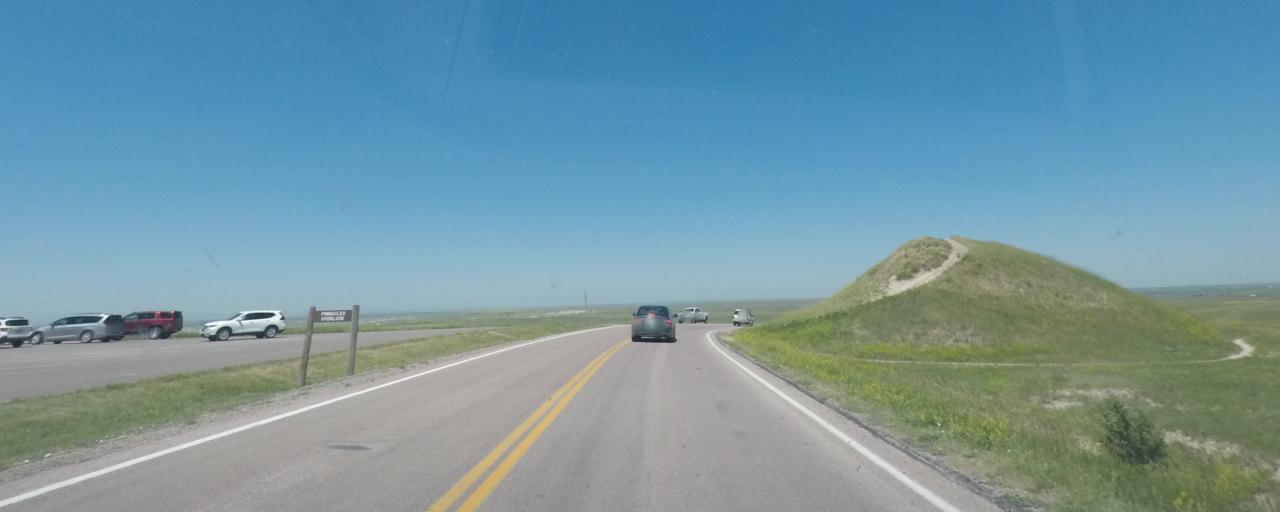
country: US
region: South Dakota
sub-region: Haakon County
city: Philip
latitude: 43.8697
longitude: -102.2327
